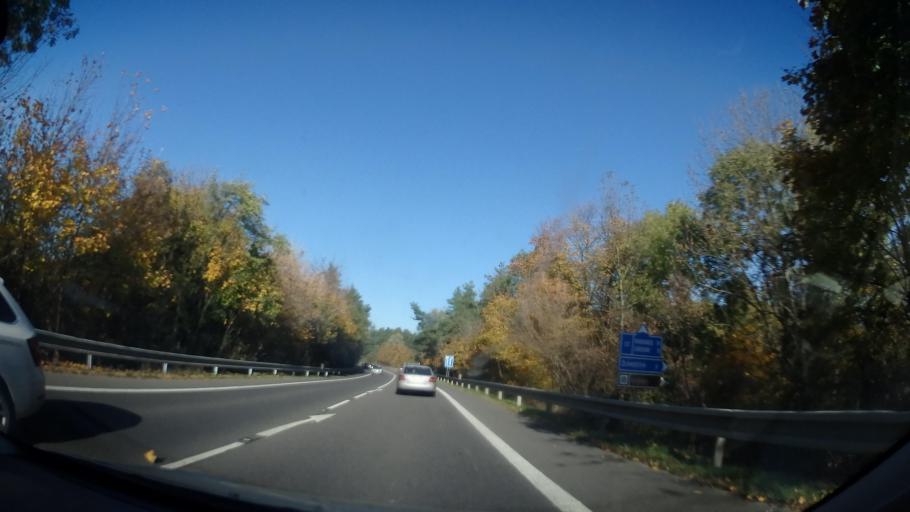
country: CZ
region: Pardubicky
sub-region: Okres Chrudim
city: Slatinany
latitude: 49.8964
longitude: 15.8257
